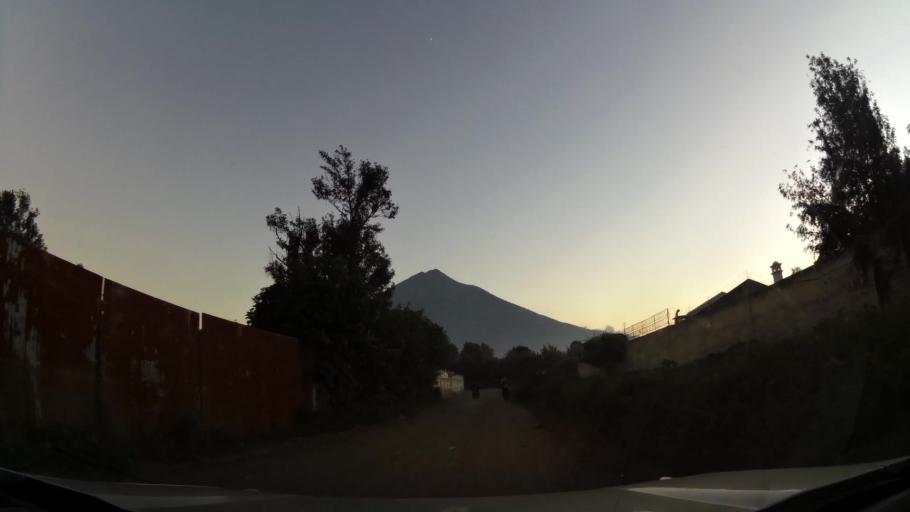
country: GT
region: Sacatepequez
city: Ciudad Vieja
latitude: 14.5439
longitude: -90.7481
